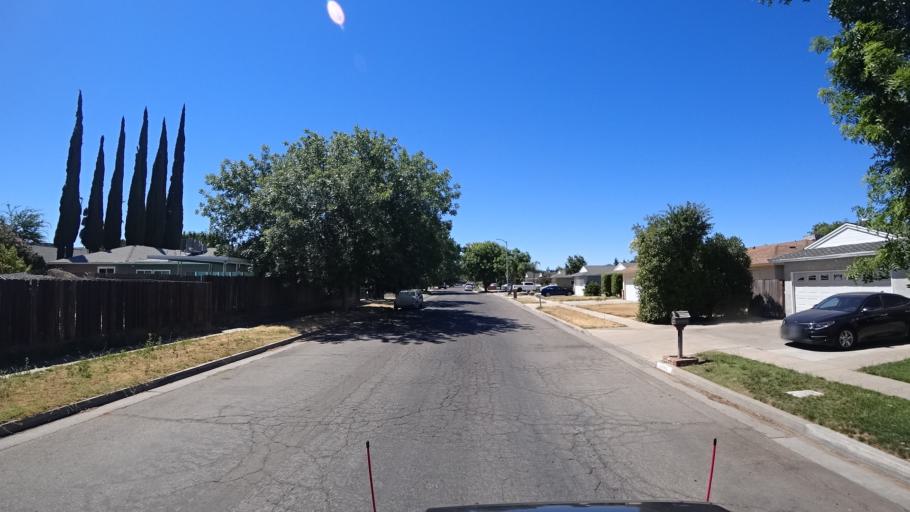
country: US
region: California
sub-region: Fresno County
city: West Park
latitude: 36.8000
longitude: -119.8484
